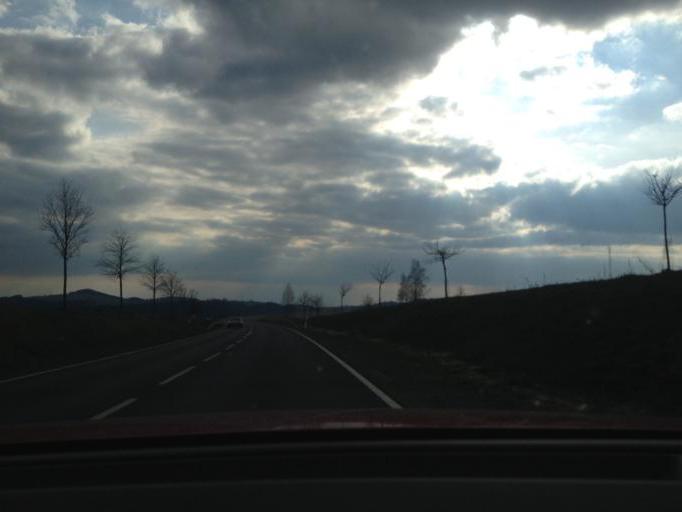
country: DE
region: Bavaria
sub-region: Upper Palatinate
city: Pullenreuth
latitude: 49.9328
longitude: 11.9939
